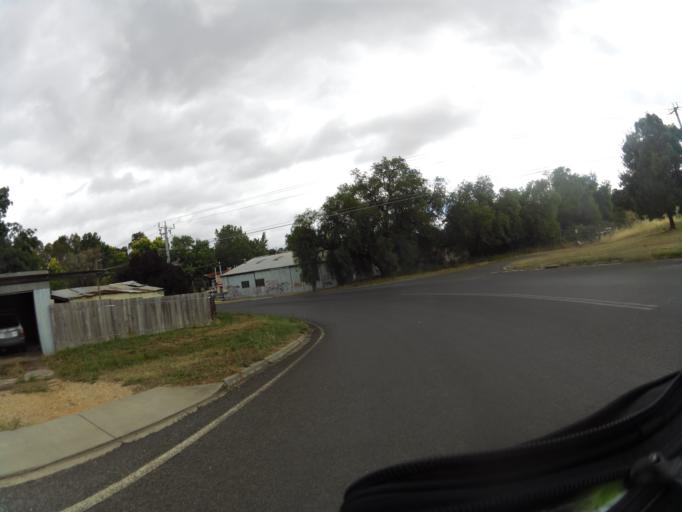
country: AU
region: Victoria
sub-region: Mount Alexander
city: Castlemaine
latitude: -37.0719
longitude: 144.2106
